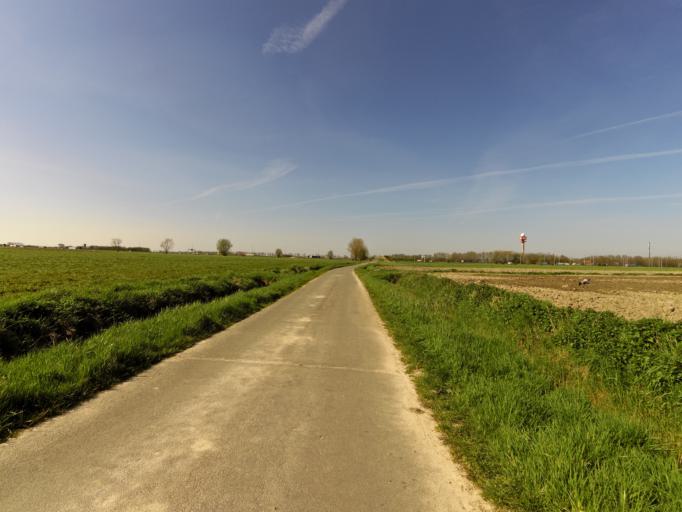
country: BE
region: Flanders
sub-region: Provincie West-Vlaanderen
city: Jabbeke
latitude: 51.1860
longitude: 3.0638
